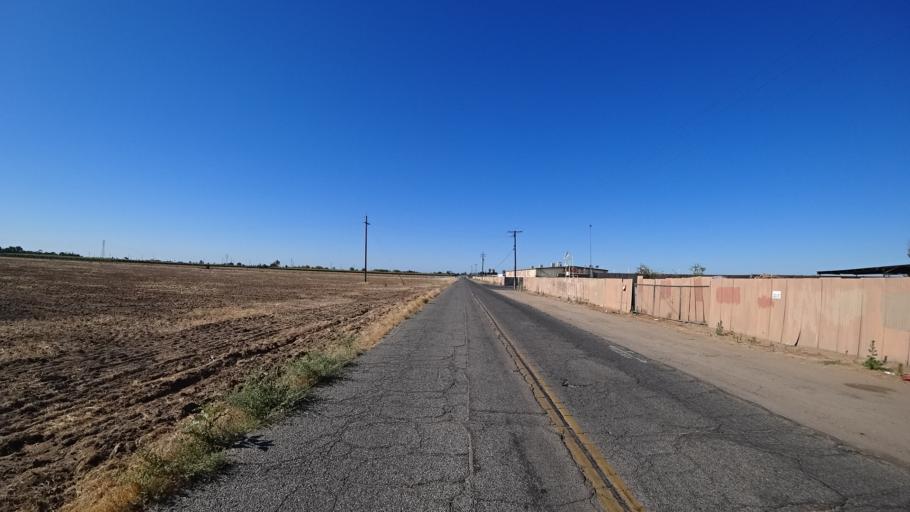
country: US
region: California
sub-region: Fresno County
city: West Park
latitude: 36.7136
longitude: -119.8268
